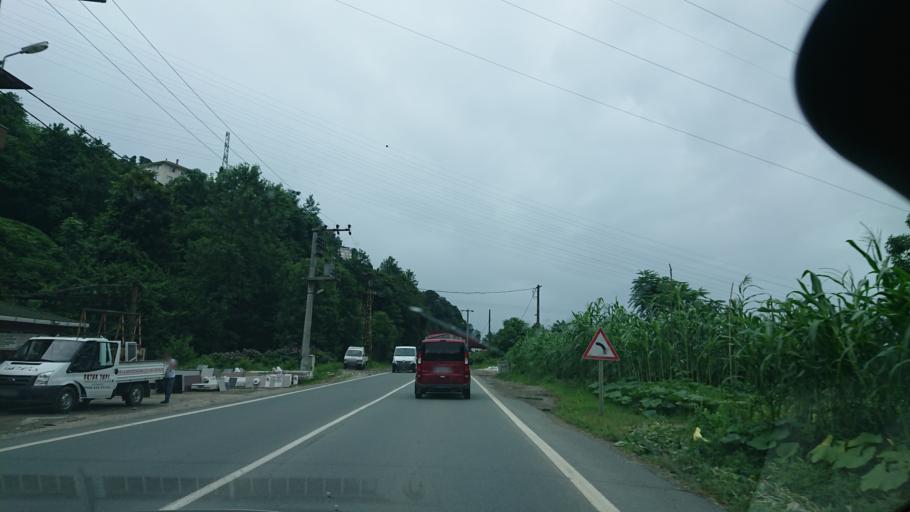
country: TR
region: Rize
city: Gundogdu
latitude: 41.0324
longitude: 40.5819
